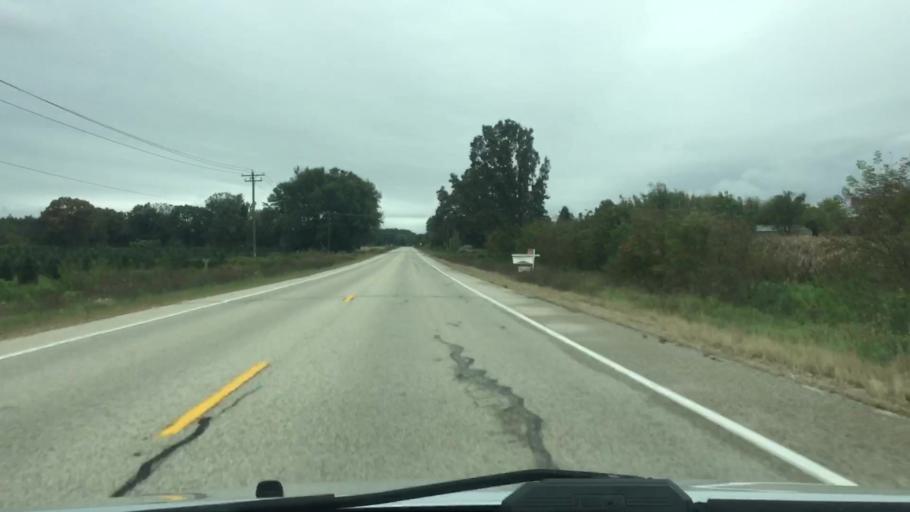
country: US
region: Wisconsin
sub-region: Jefferson County
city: Palmyra
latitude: 42.8238
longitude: -88.5555
